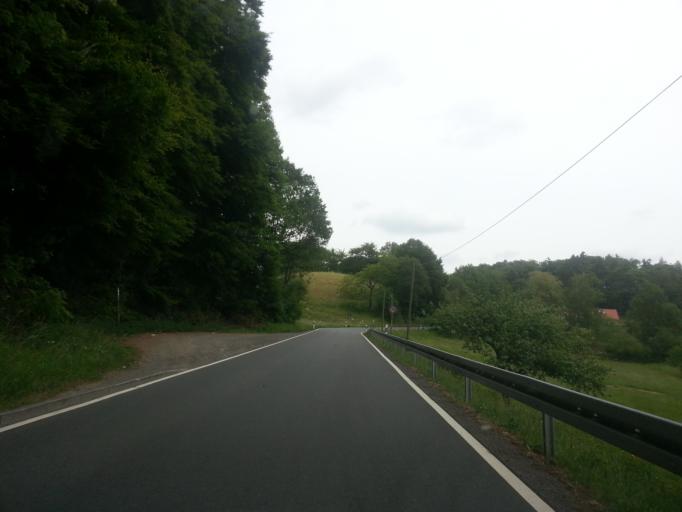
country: DE
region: Hesse
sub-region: Regierungsbezirk Darmstadt
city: Seeheim-Jugenheim
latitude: 49.7341
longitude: 8.6765
